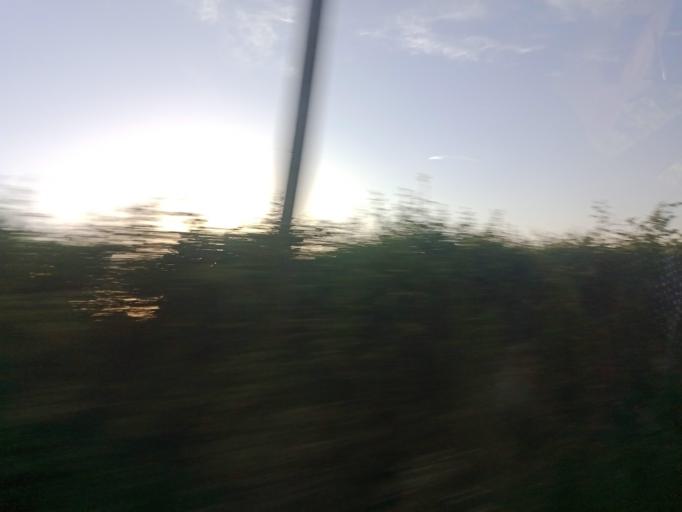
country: IE
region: Leinster
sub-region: Kilkenny
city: Castlecomer
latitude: 52.7377
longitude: -7.2375
